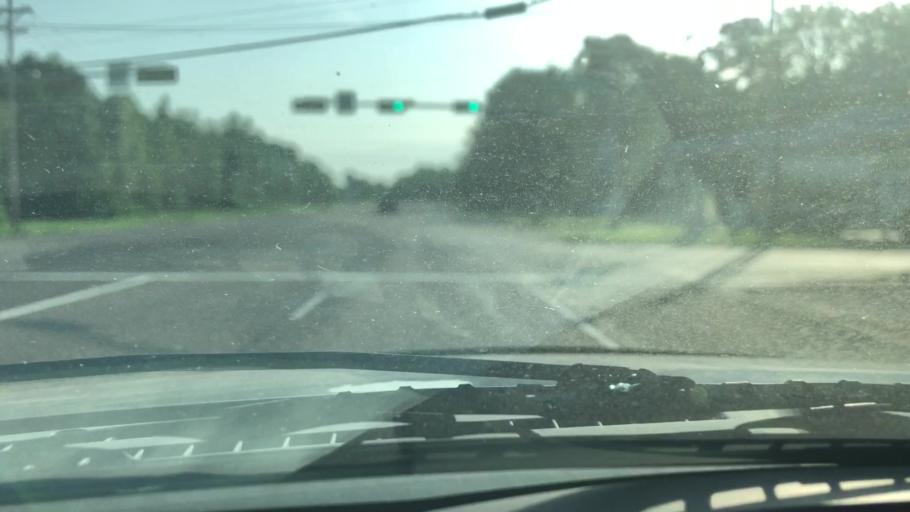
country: US
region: Texas
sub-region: Bowie County
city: Texarkana
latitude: 33.4032
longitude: -94.0651
